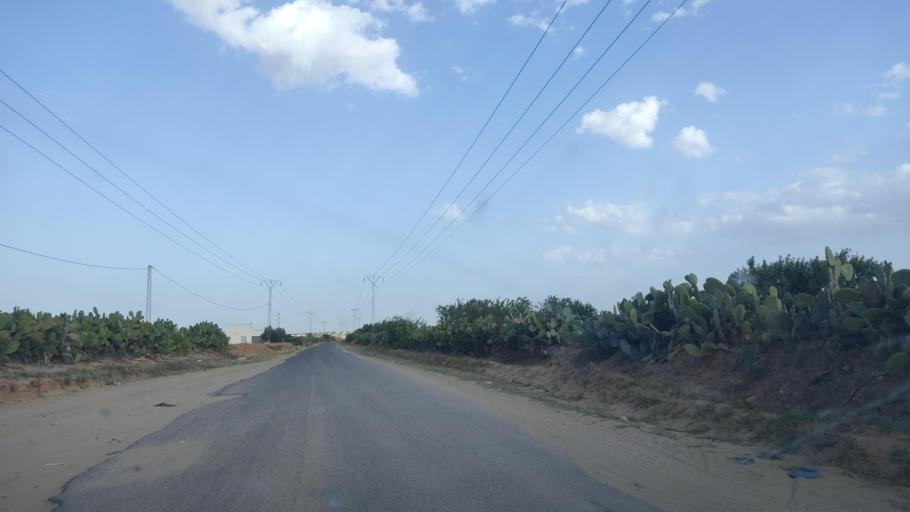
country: TN
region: Safaqis
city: Sfax
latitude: 34.8559
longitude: 10.6056
